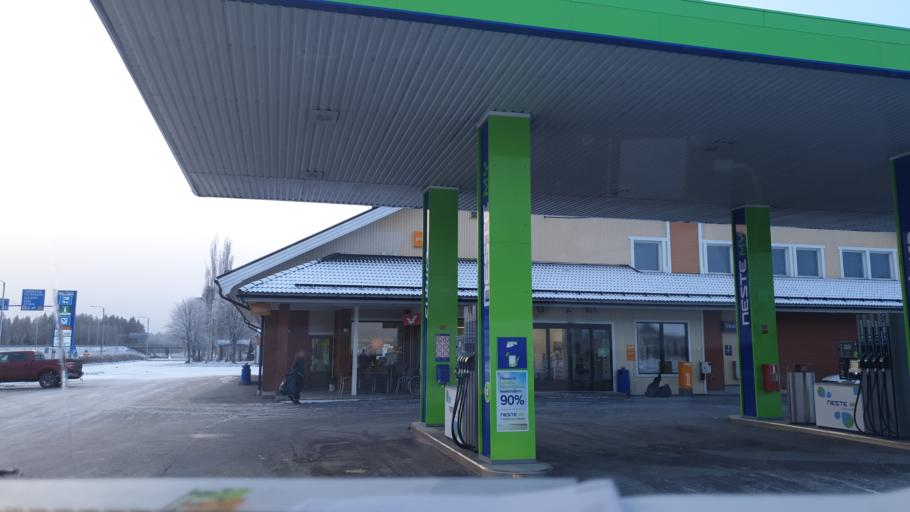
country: FI
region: Ostrobothnia
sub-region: Jakobstadsregionen
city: Bennaes
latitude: 63.6329
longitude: 22.8577
